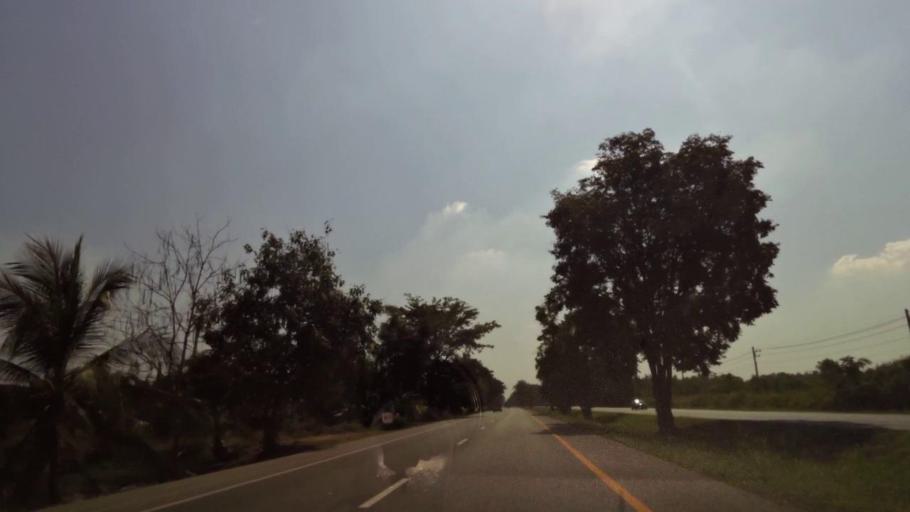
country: TH
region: Phichit
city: Bueng Na Rang
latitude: 16.2369
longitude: 100.1255
